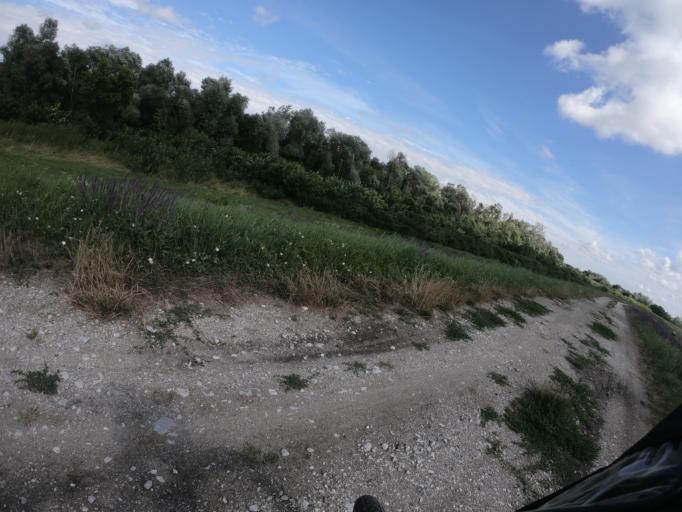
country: HU
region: Heves
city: Poroszlo
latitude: 47.6934
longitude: 20.6864
